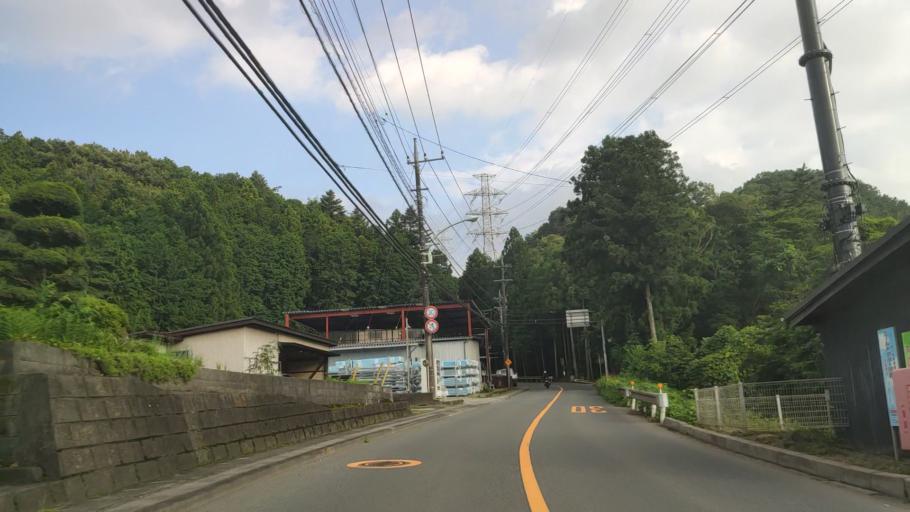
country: JP
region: Saitama
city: Hanno
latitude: 35.8308
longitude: 139.2700
